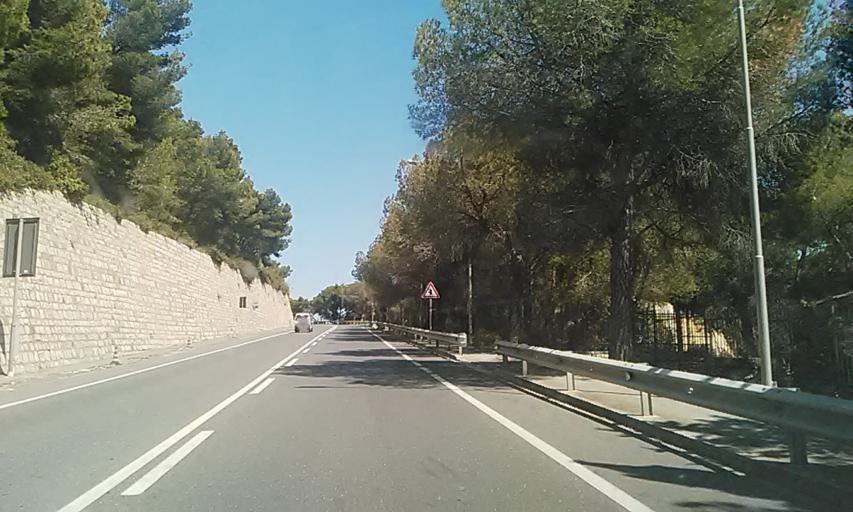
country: IT
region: Liguria
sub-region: Provincia di Savona
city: Marina di Andora
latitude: 43.9529
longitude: 8.1629
